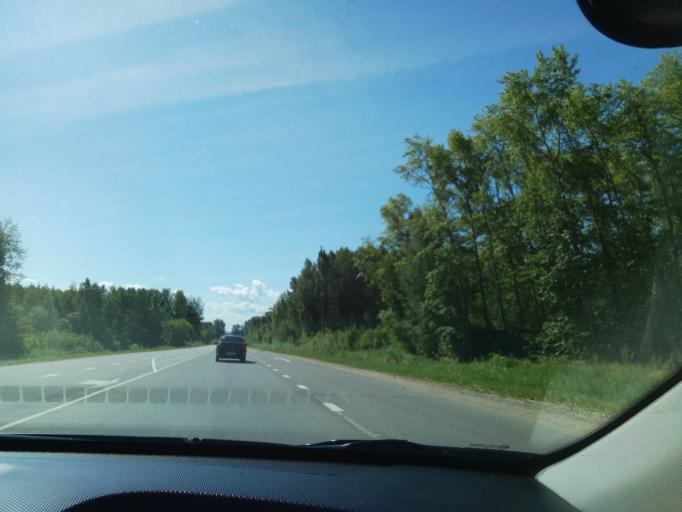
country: RU
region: Chuvashia
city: Novocheboksarsk
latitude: 56.0776
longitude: 47.4966
